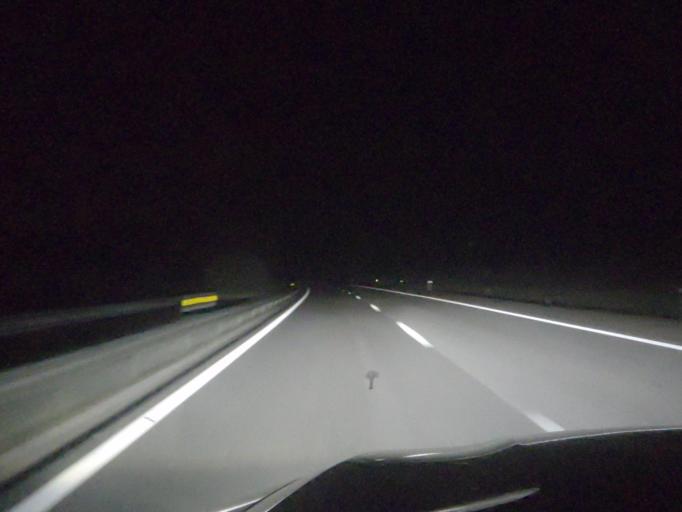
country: PT
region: Aveiro
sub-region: Aveiro
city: Eixo
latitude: 40.6009
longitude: -8.5548
